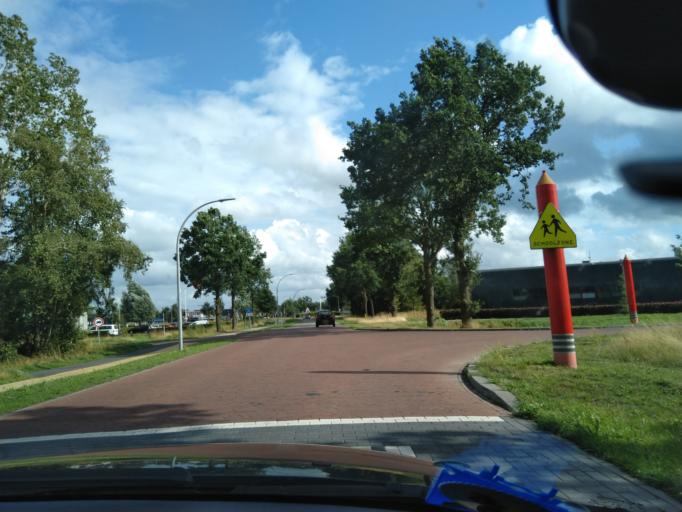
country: NL
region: Groningen
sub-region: Gemeente Zuidhorn
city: Zuidhorn
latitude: 53.2507
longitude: 6.4055
